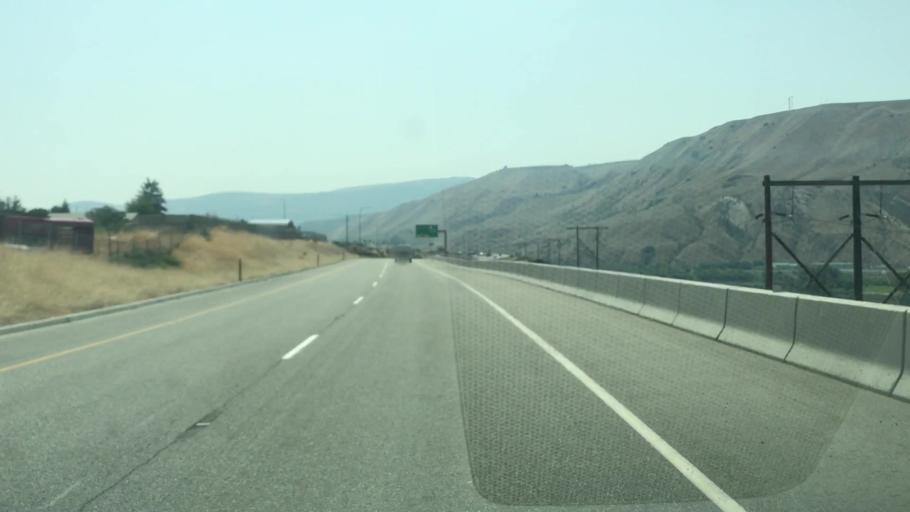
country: US
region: Washington
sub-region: Douglas County
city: East Wenatchee
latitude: 47.4034
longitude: -120.2909
